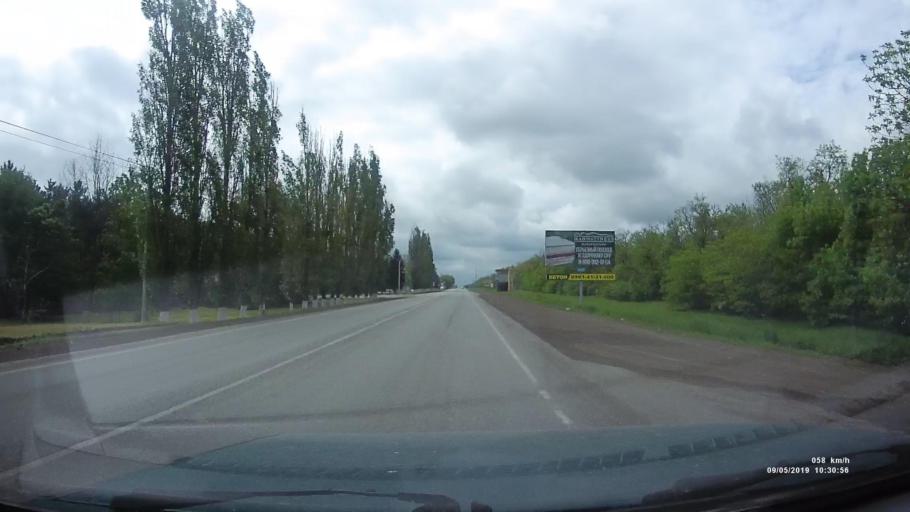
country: RU
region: Rostov
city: Azov
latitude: 47.0862
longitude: 39.4285
